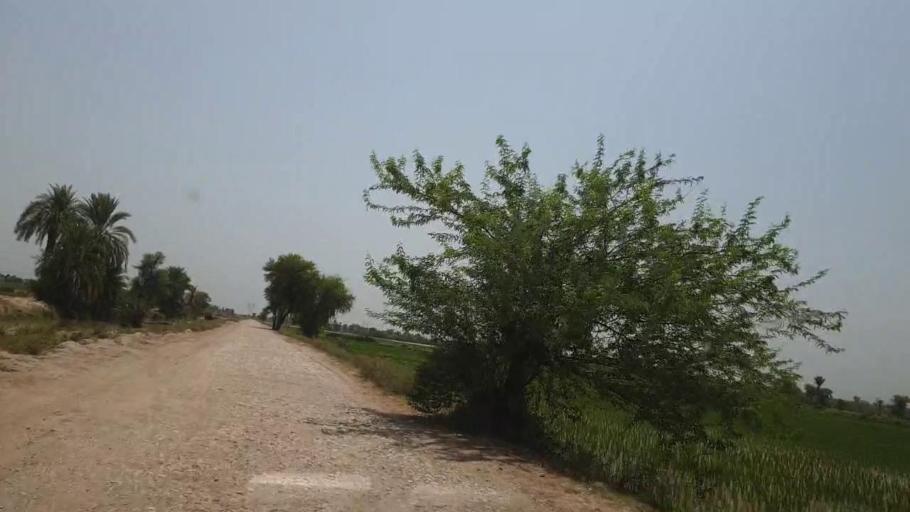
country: PK
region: Sindh
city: Lakhi
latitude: 27.8659
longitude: 68.6068
